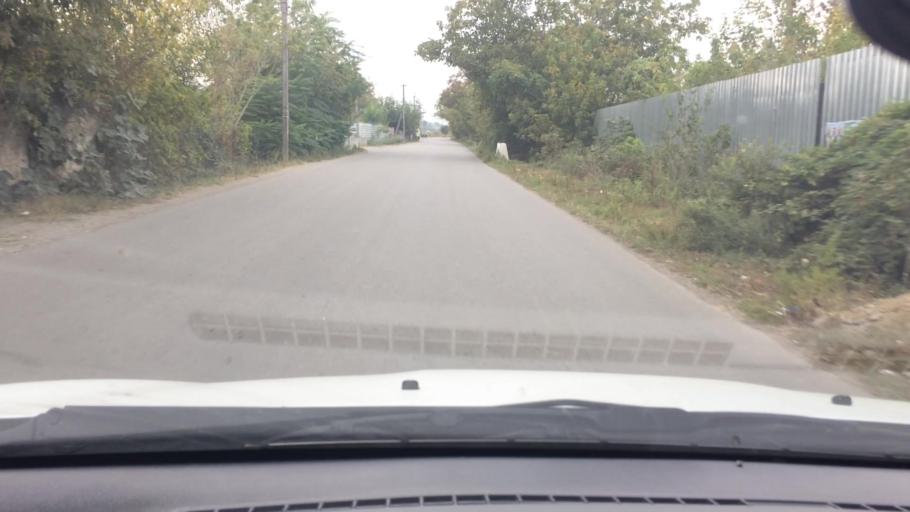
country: AM
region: Tavush
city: Bagratashen
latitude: 41.3384
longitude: 44.9240
